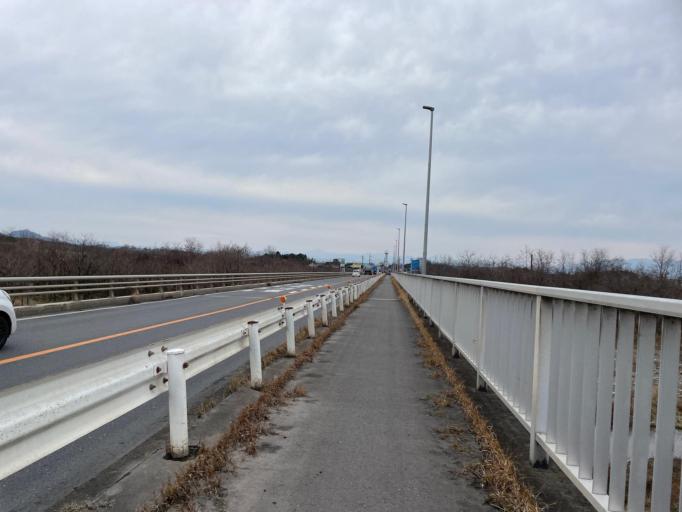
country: JP
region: Gunma
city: Fujioka
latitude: 36.2378
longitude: 139.0948
